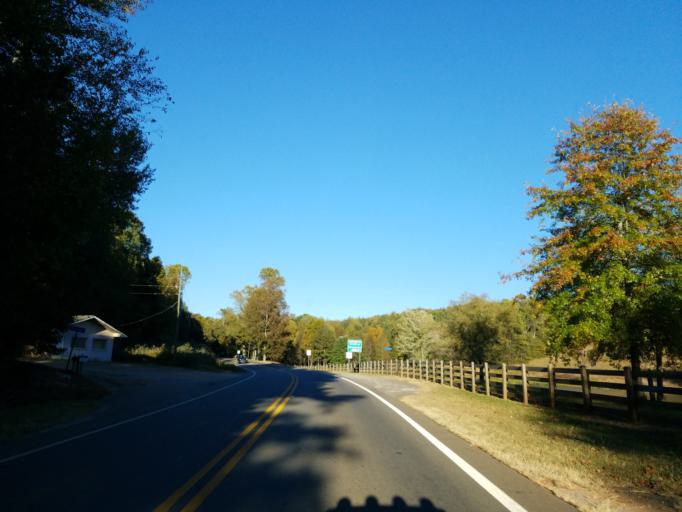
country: US
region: Georgia
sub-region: Pickens County
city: Nelson
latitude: 34.4162
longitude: -84.2570
